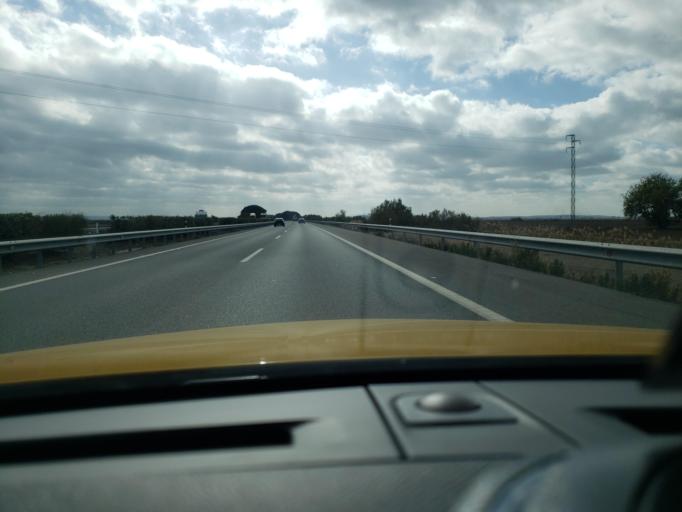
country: ES
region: Andalusia
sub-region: Provincia de Sevilla
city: Los Palacios y Villafranca
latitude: 37.0738
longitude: -5.9366
